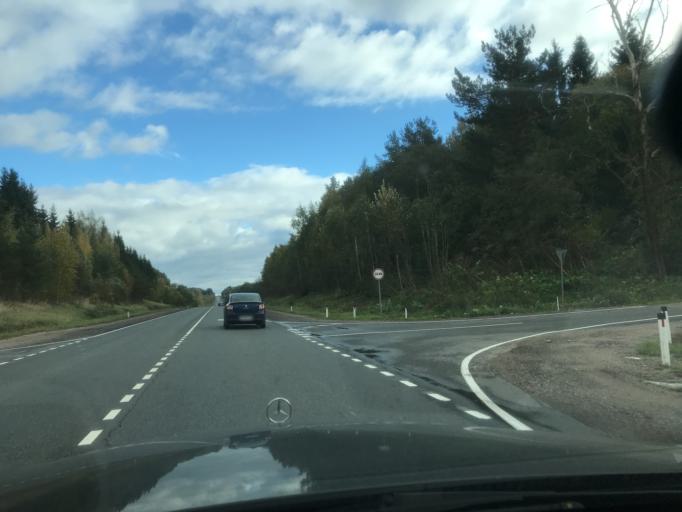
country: RU
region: Pskov
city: Opochka
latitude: 56.6547
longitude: 28.7590
